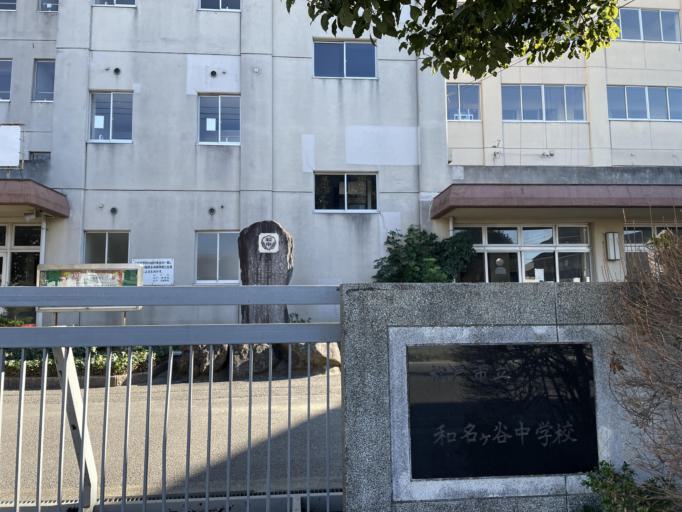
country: JP
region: Chiba
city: Matsudo
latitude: 35.7768
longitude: 139.9166
